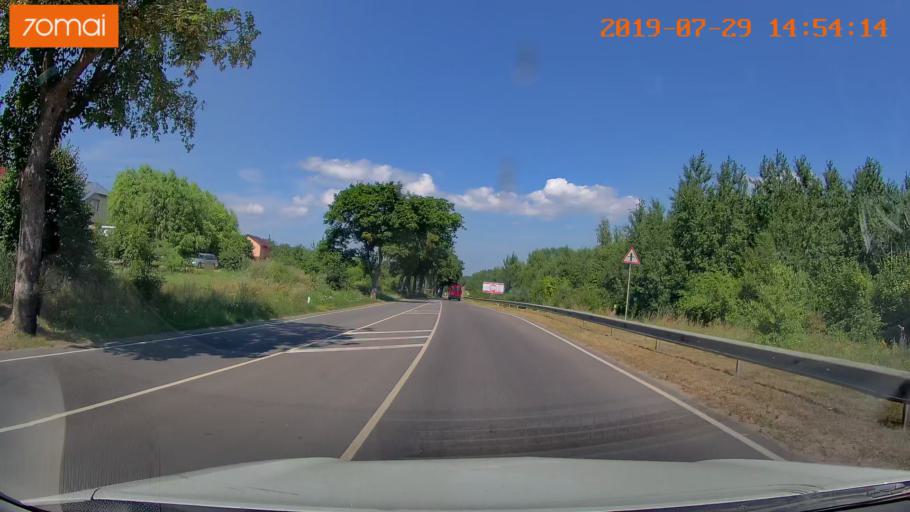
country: RU
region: Kaliningrad
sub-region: Gorod Kaliningrad
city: Baltiysk
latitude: 54.6723
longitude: 19.9235
